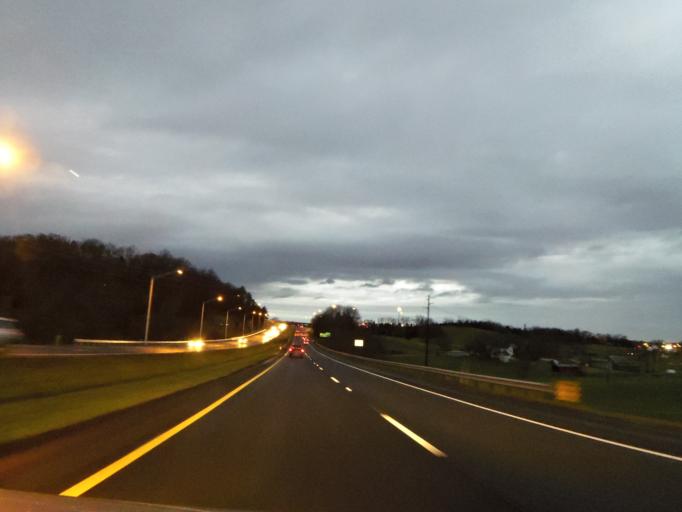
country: US
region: Tennessee
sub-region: Washington County
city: Gray
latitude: 36.4027
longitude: -82.4689
